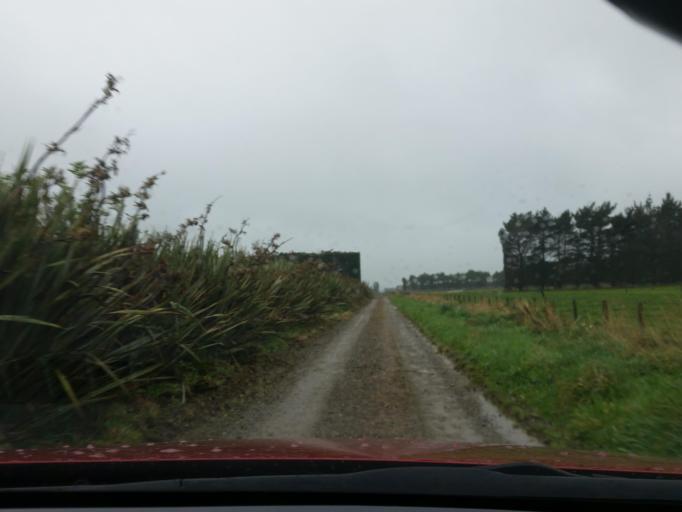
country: NZ
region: Southland
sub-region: Invercargill City
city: Invercargill
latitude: -46.3387
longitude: 168.4229
